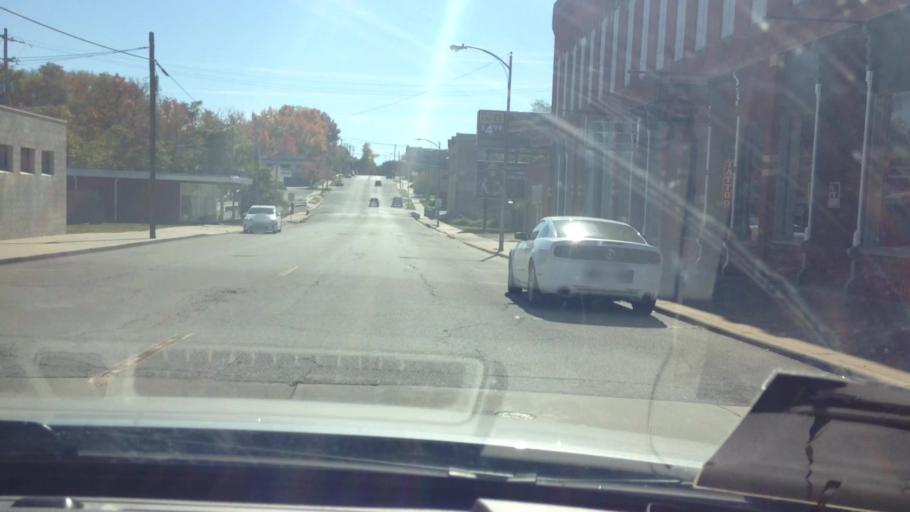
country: US
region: Kansas
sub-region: Leavenworth County
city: Leavenworth
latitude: 39.3162
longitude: -94.9150
